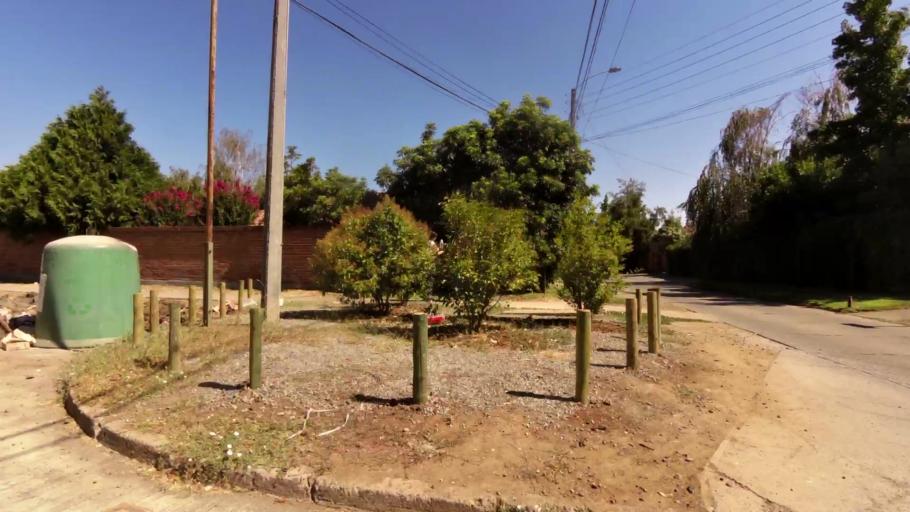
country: CL
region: Maule
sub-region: Provincia de Talca
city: Talca
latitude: -35.4314
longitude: -71.6163
